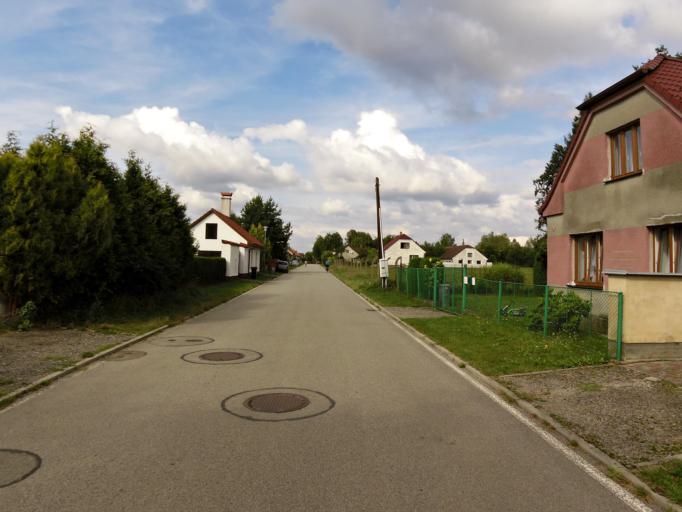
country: CZ
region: Jihocesky
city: Suchdol nad Luznici
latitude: 48.9067
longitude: 14.9139
